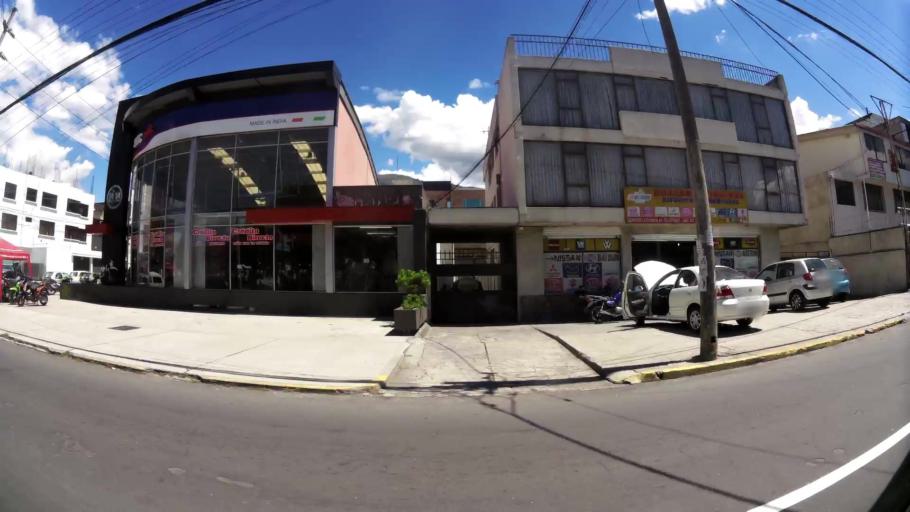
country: EC
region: Pichincha
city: Quito
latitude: -0.1617
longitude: -78.4859
